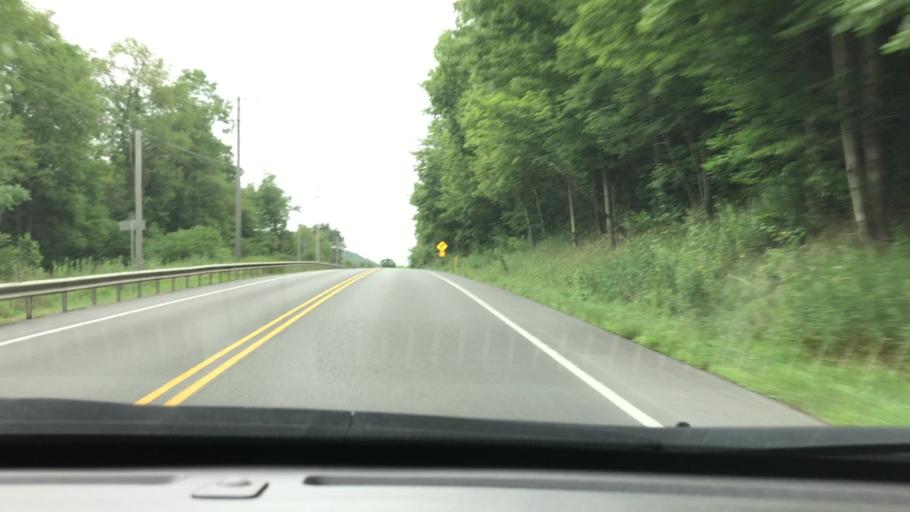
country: US
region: Pennsylvania
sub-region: Elk County
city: Johnsonburg
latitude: 41.5842
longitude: -78.6875
